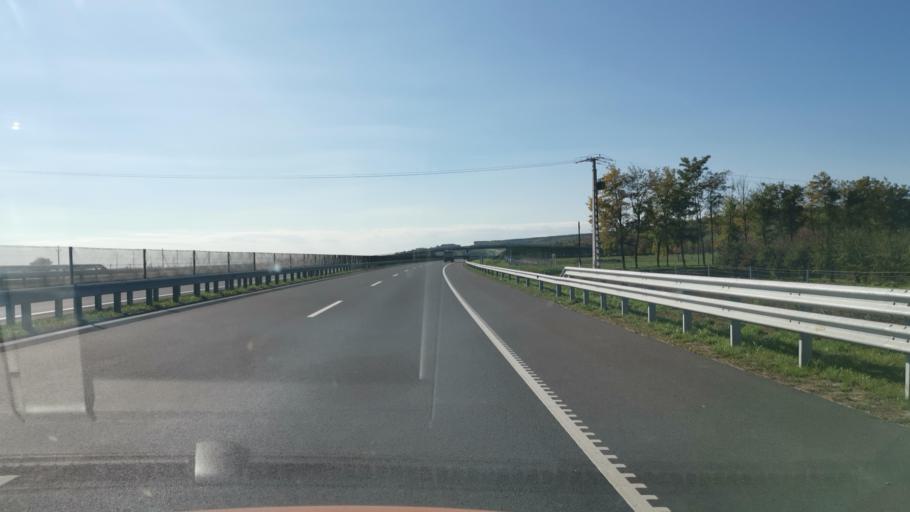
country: HU
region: Borsod-Abauj-Zemplen
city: Aszalo
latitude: 48.2416
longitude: 20.9690
